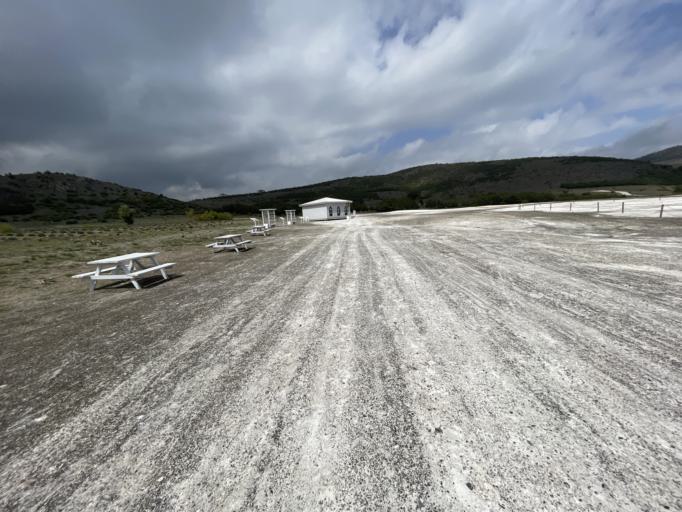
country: TR
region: Burdur
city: Yesilova
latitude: 37.5335
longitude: 29.6434
